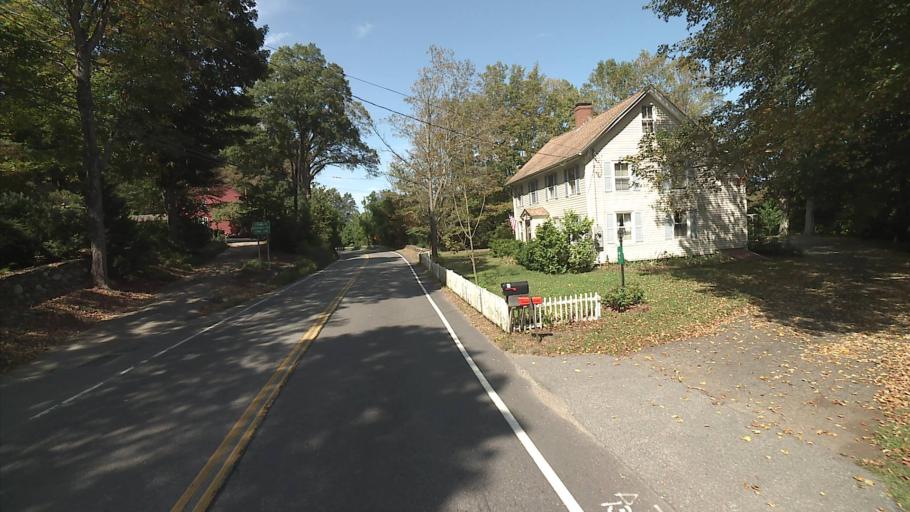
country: US
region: Connecticut
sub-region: New London County
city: Baltic
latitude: 41.5765
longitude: -72.1387
